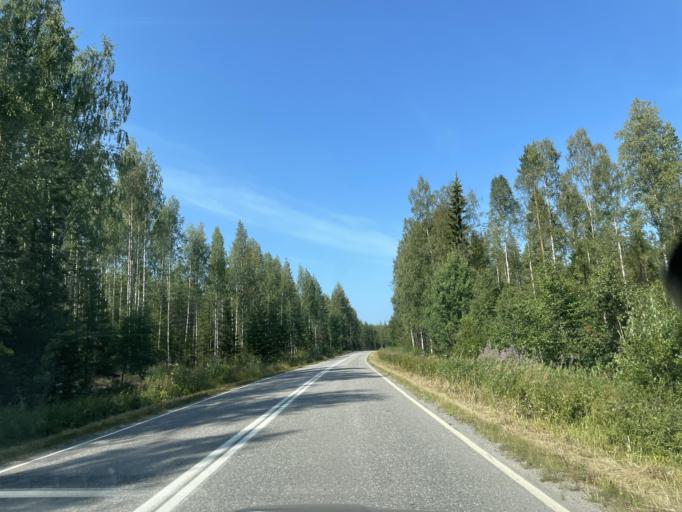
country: FI
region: Central Finland
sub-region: Saarijaervi-Viitasaari
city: Pihtipudas
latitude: 63.3653
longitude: 25.6979
